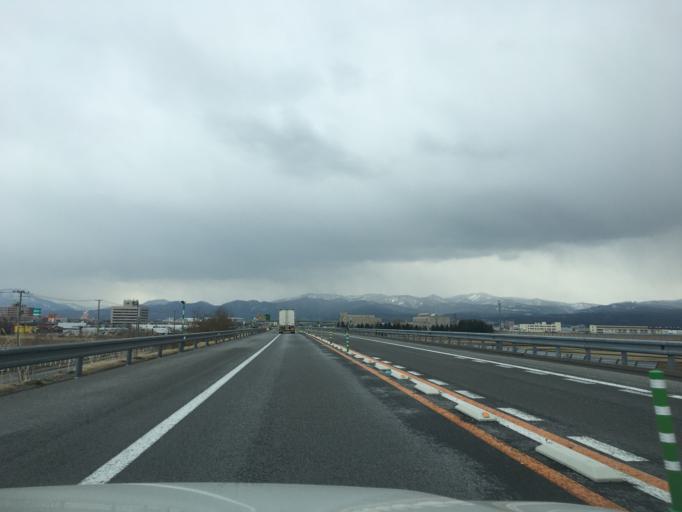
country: JP
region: Aomori
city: Aomori Shi
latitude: 40.7973
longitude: 140.7301
